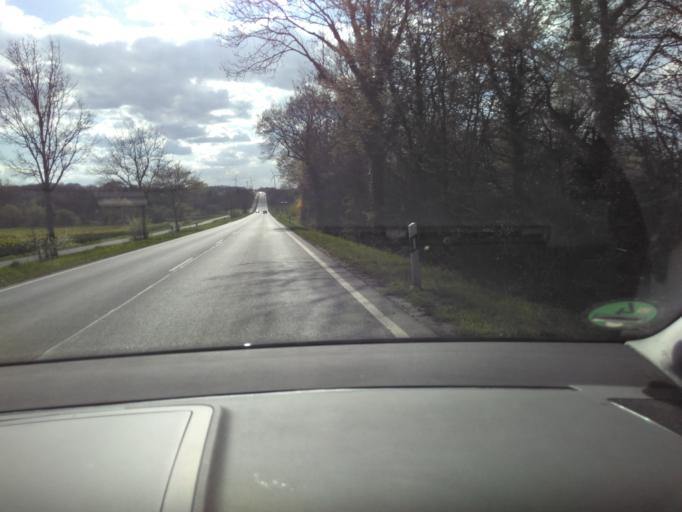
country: DE
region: North Rhine-Westphalia
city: Oelde
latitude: 51.7827
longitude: 8.1387
